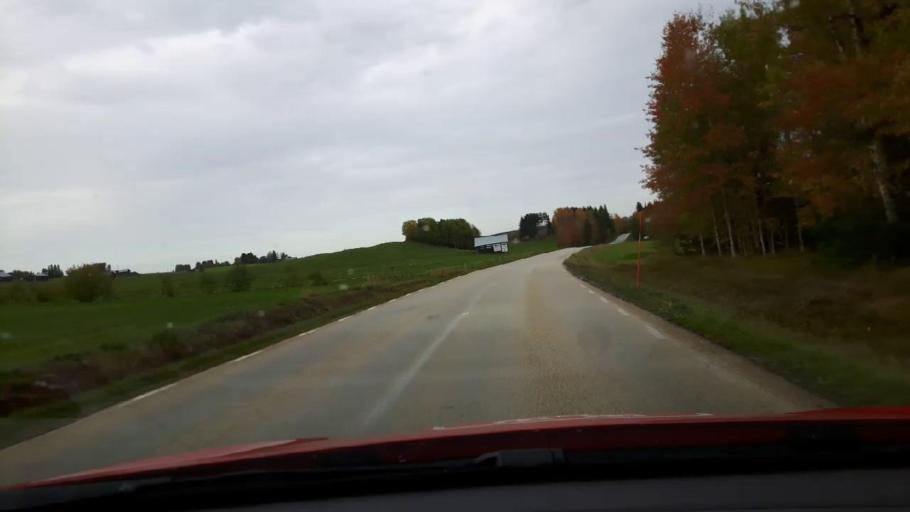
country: SE
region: Jaemtland
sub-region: Bergs Kommun
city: Hoverberg
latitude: 62.9878
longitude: 14.3395
